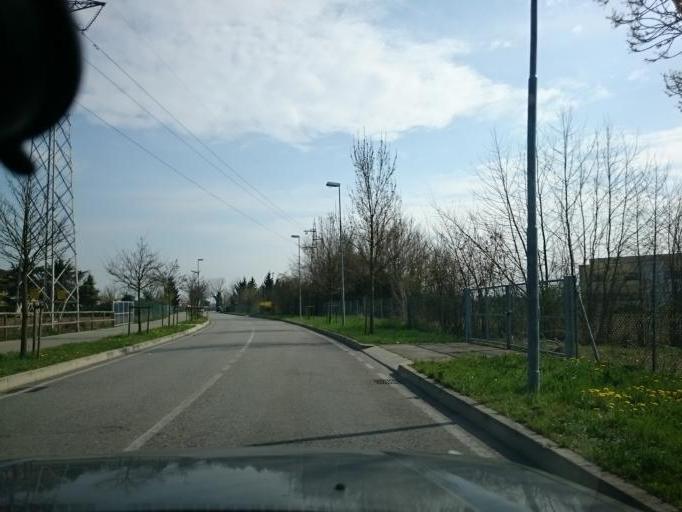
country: IT
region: Veneto
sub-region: Provincia di Padova
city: Mandriola-Sant'Agostino
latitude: 45.3731
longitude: 11.8674
